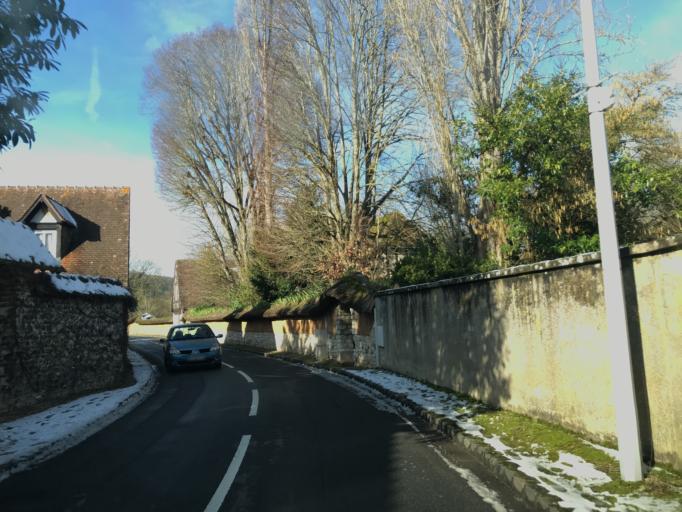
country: FR
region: Haute-Normandie
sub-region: Departement de l'Eure
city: Houlbec-Cocherel
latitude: 49.0689
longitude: 1.2901
